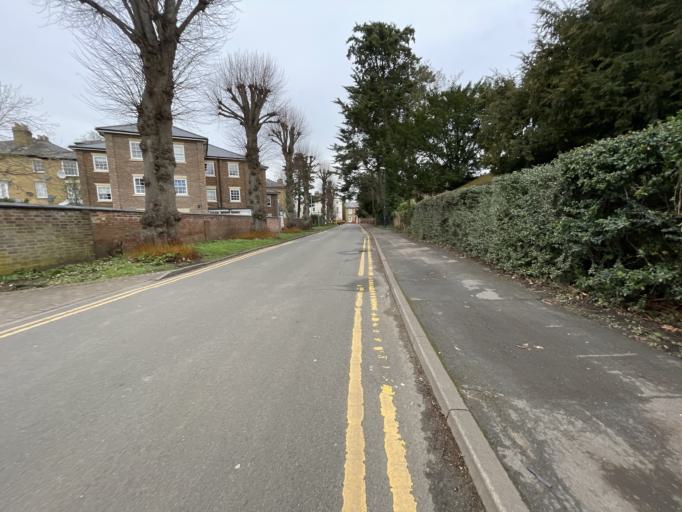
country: GB
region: England
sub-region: Warwickshire
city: Rugby
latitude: 52.3691
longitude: -1.2685
